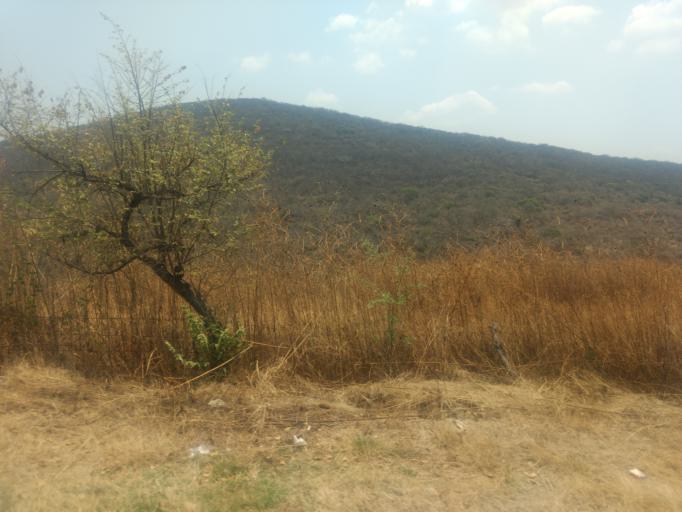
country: MX
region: Morelos
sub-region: Mazatepec
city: Cuauchichinola
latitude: 18.6530
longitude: -99.4043
